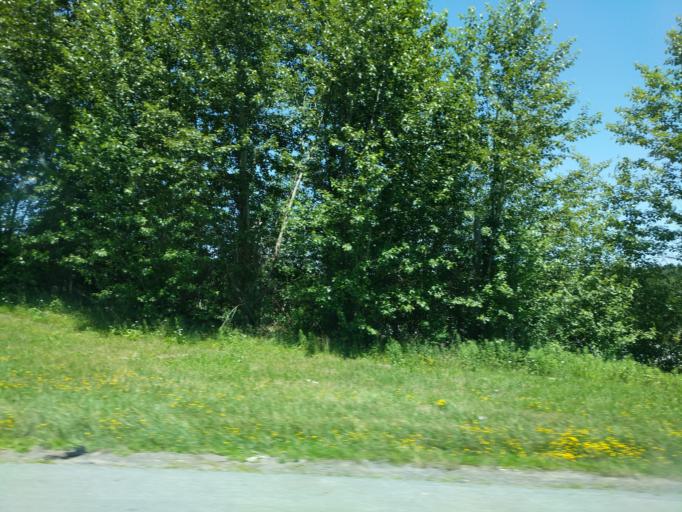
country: US
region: New York
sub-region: Sullivan County
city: Monticello
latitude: 41.6891
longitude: -74.7276
